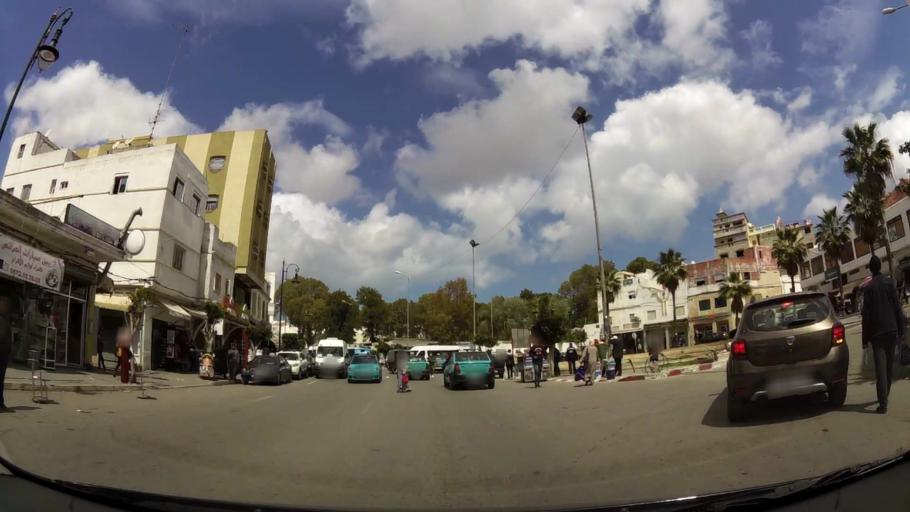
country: MA
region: Tanger-Tetouan
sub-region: Tanger-Assilah
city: Tangier
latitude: 35.7565
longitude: -5.8106
